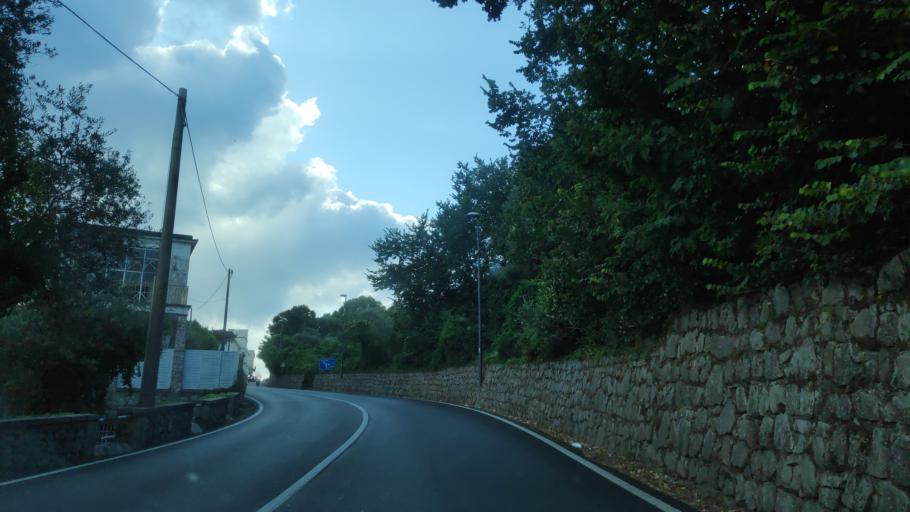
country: IT
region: Campania
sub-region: Provincia di Napoli
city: Piano di Sorrento
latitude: 40.6183
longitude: 14.4250
